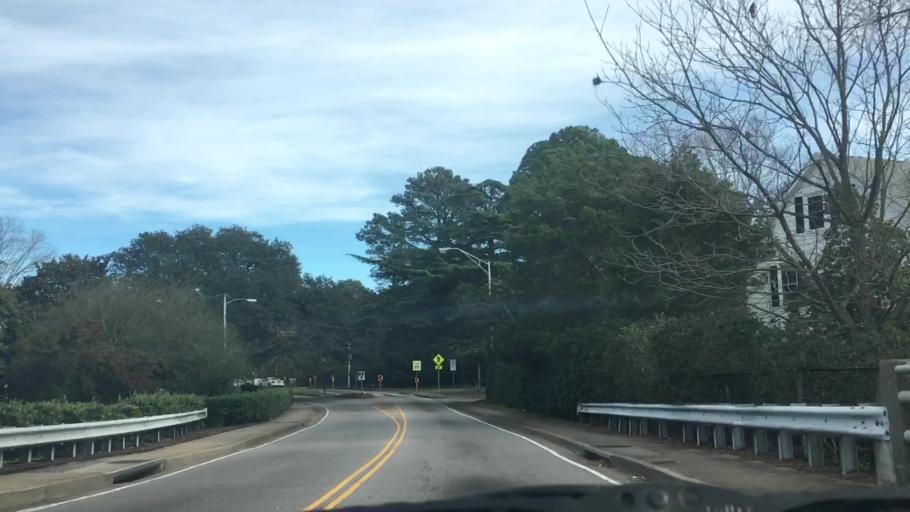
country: US
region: Virginia
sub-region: City of Norfolk
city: Norfolk
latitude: 36.8889
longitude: -76.2749
